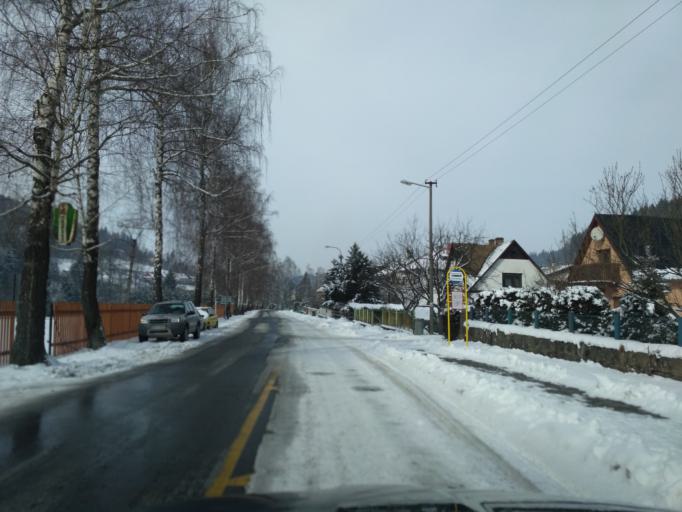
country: CZ
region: Zlin
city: Valasska Bystrice
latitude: 49.4102
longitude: 18.1155
